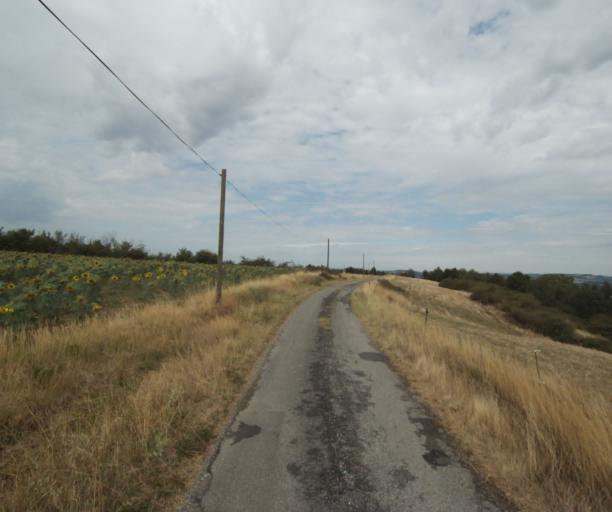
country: FR
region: Midi-Pyrenees
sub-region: Departement de la Haute-Garonne
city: Revel
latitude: 43.4392
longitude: 1.9881
